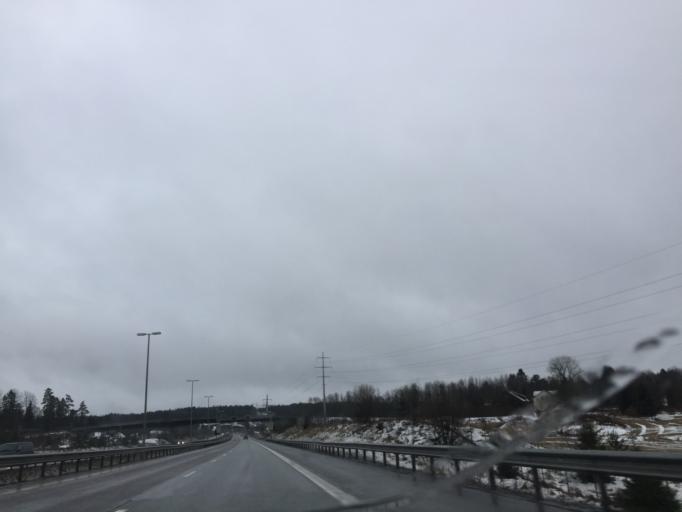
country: NO
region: Akershus
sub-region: Vestby
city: Vestby
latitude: 59.5450
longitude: 10.7241
